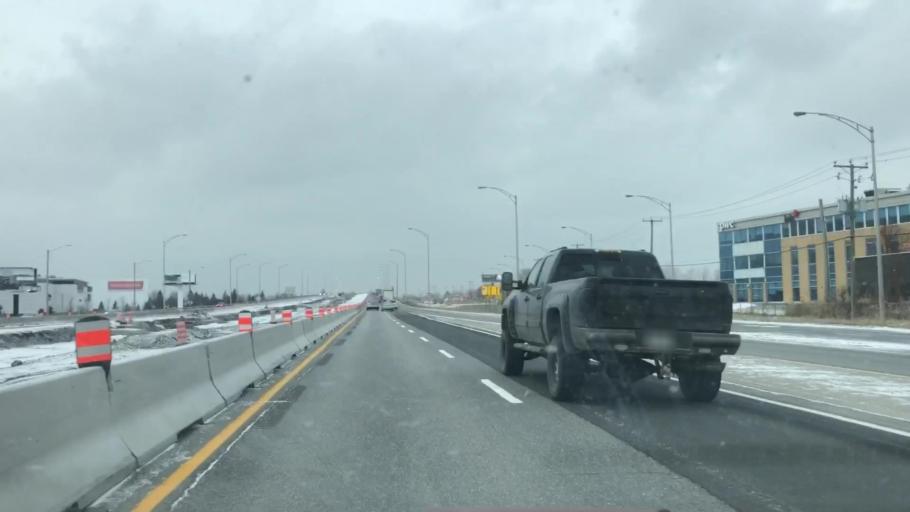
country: CA
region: Quebec
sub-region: Monteregie
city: Brossard
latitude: 45.4519
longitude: -73.4401
